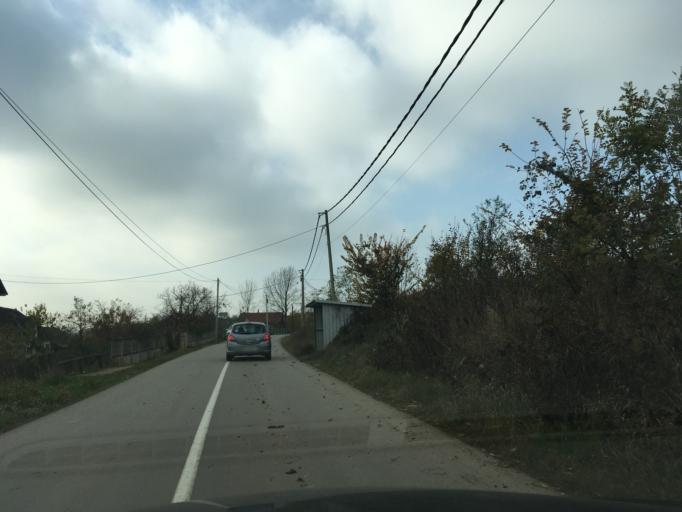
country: RS
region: Central Serbia
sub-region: Belgrade
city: Sopot
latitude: 44.4957
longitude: 20.6033
